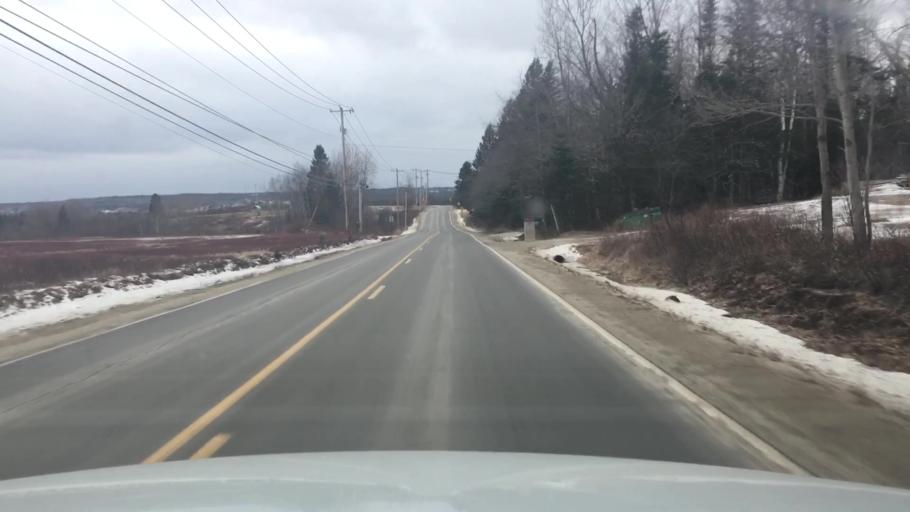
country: US
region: Maine
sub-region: Washington County
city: Addison
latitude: 44.6211
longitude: -67.7072
